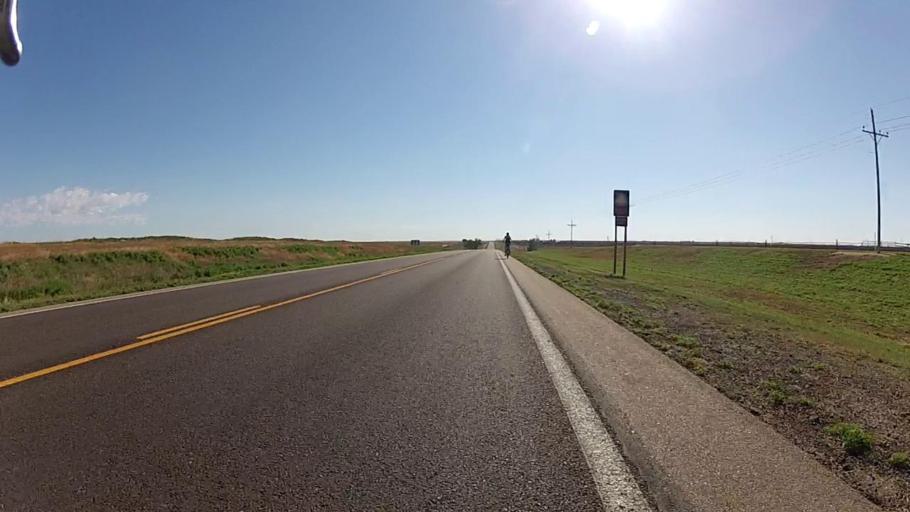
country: US
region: Kansas
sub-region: Haskell County
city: Sublette
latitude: 37.5637
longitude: -100.5595
